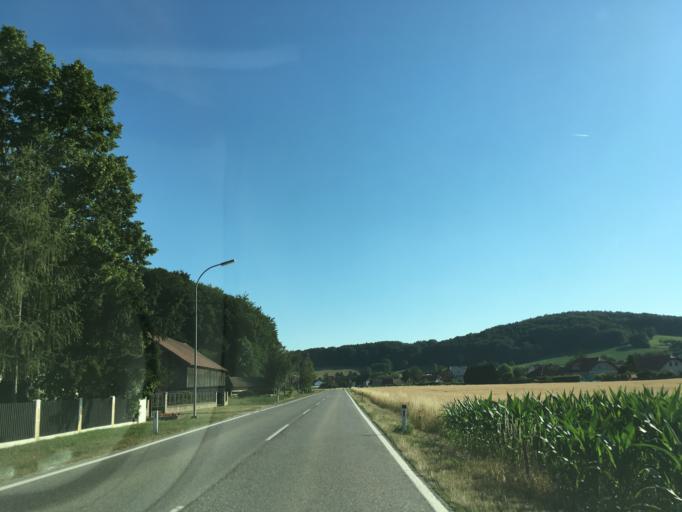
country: AT
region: Lower Austria
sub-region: Politischer Bezirk Sankt Polten
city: Boheimkirchen
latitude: 48.1738
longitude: 15.7559
